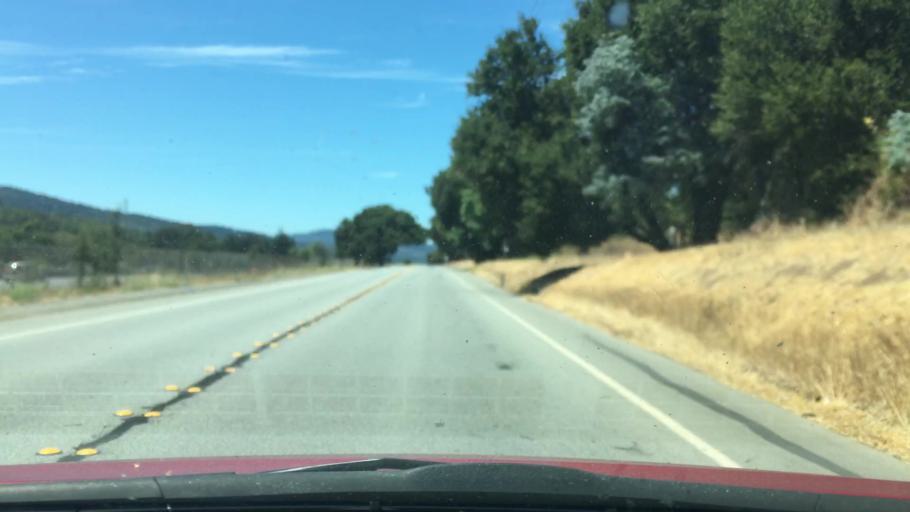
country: US
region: California
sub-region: San Mateo County
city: Emerald Lake Hills
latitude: 37.4517
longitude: -122.2801
